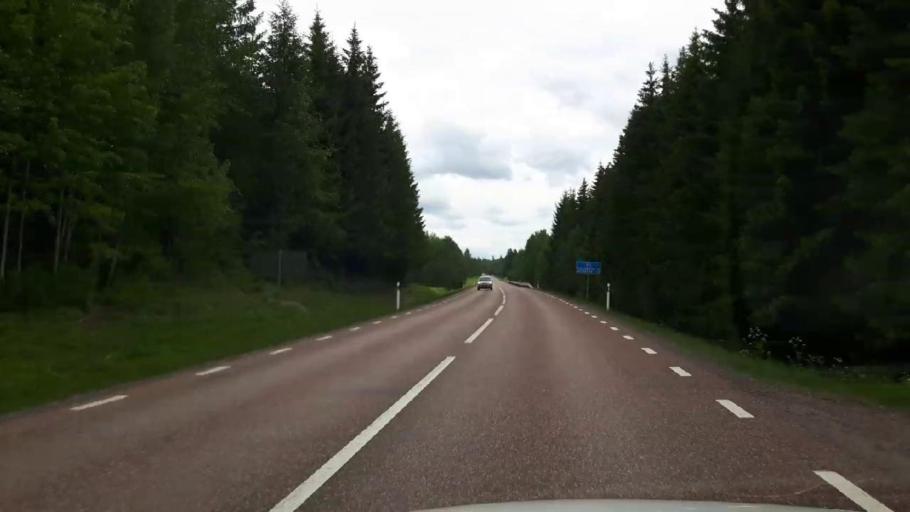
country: SE
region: Dalarna
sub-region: Hedemora Kommun
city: Brunna
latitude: 60.2079
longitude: 15.9917
